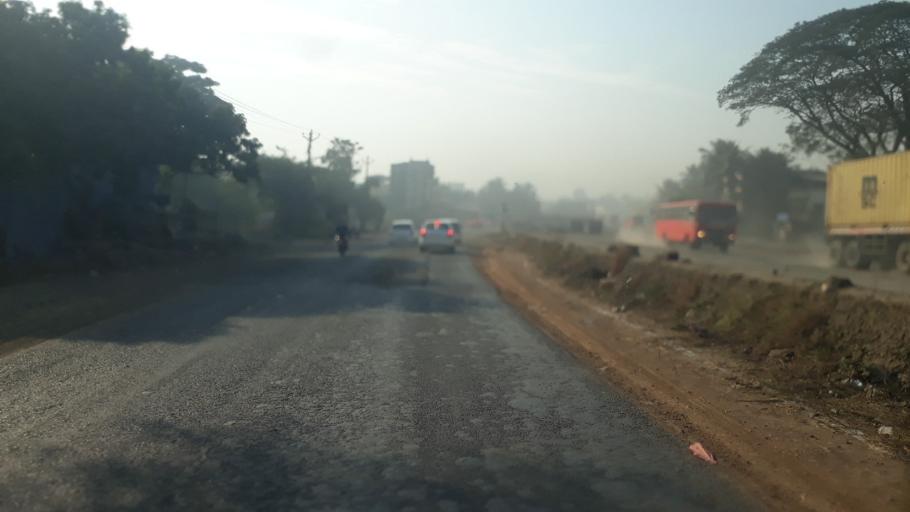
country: IN
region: Maharashtra
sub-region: Raigarh
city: Kalundri
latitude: 18.9614
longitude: 73.1312
